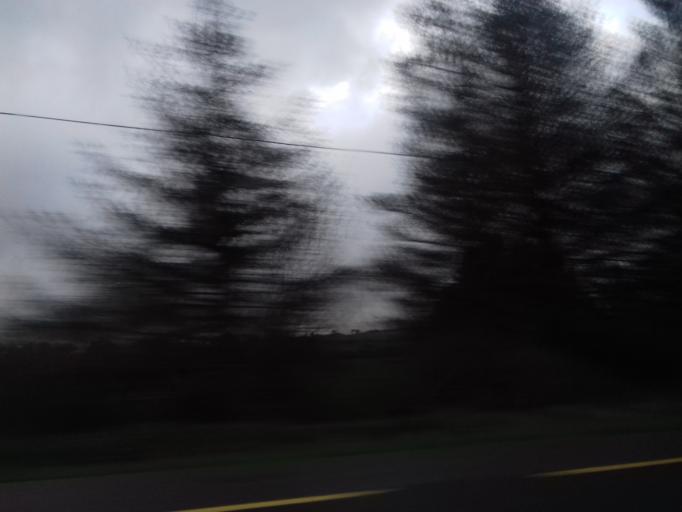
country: IE
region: Munster
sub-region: County Limerick
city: Abbeyfeale
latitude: 52.3038
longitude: -9.3806
